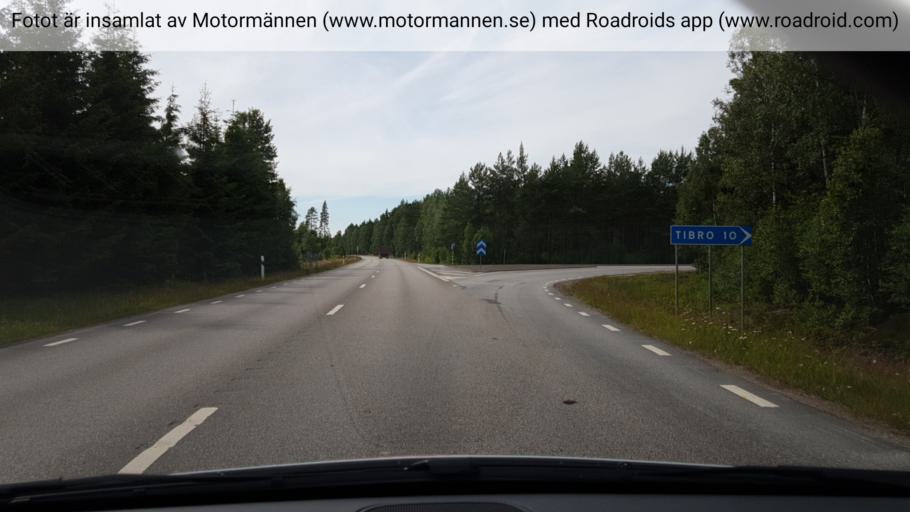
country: SE
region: Vaestra Goetaland
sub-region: Hjo Kommun
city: Hjo
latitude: 58.3397
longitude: 14.2287
